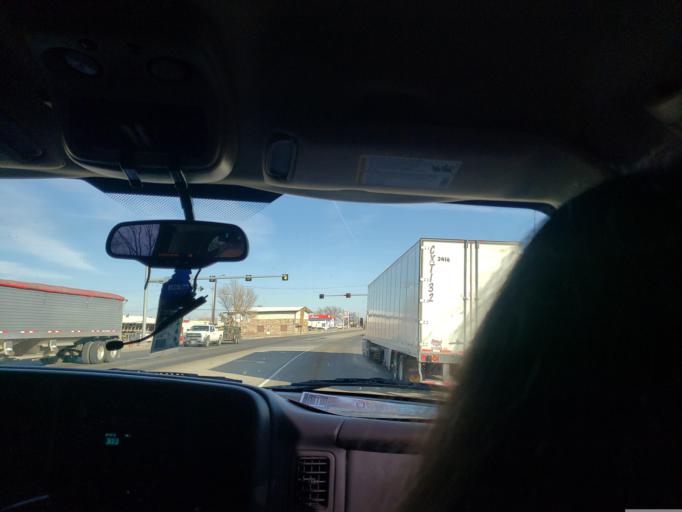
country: US
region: Oklahoma
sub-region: Texas County
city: Goodwell
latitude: 36.5018
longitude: -101.7840
